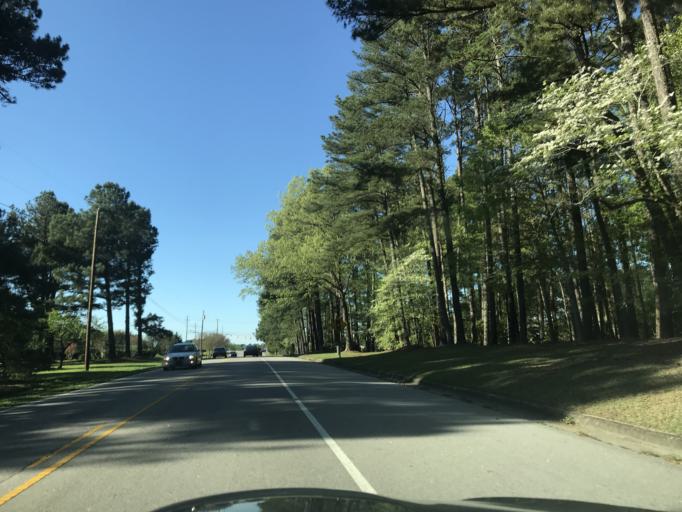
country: US
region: North Carolina
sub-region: Wake County
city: Knightdale
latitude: 35.8319
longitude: -78.5555
